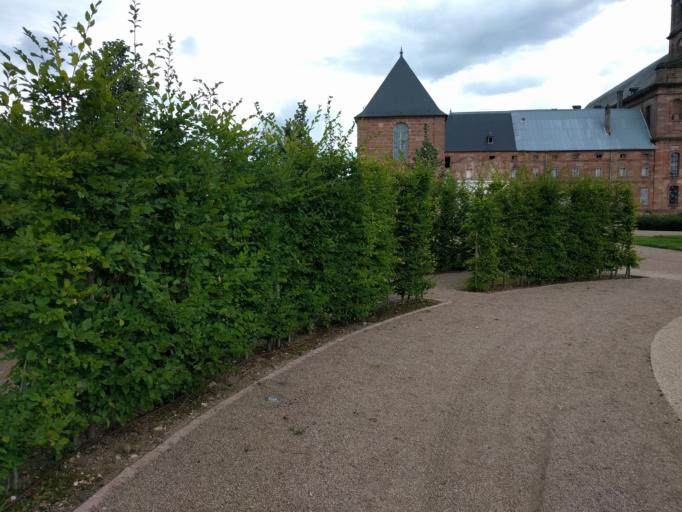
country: FR
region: Lorraine
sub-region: Departement des Vosges
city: Moyenmoutier
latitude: 48.3788
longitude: 6.9107
